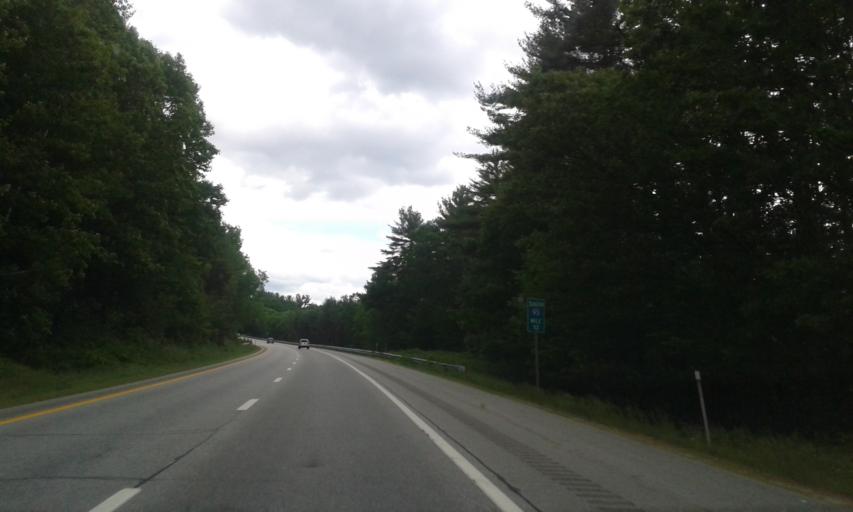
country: US
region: New Hampshire
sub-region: Merrimack County
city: Northfield
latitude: 43.3899
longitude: -71.6053
